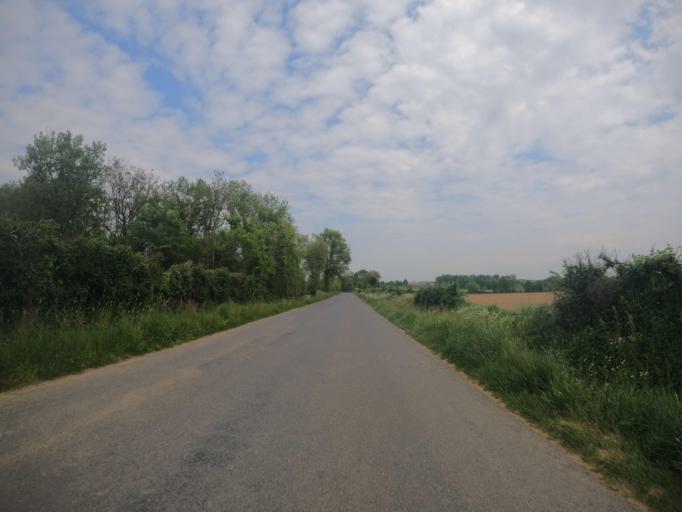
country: FR
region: Poitou-Charentes
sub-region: Departement des Deux-Sevres
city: Saint-Varent
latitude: 46.8742
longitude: -0.2879
